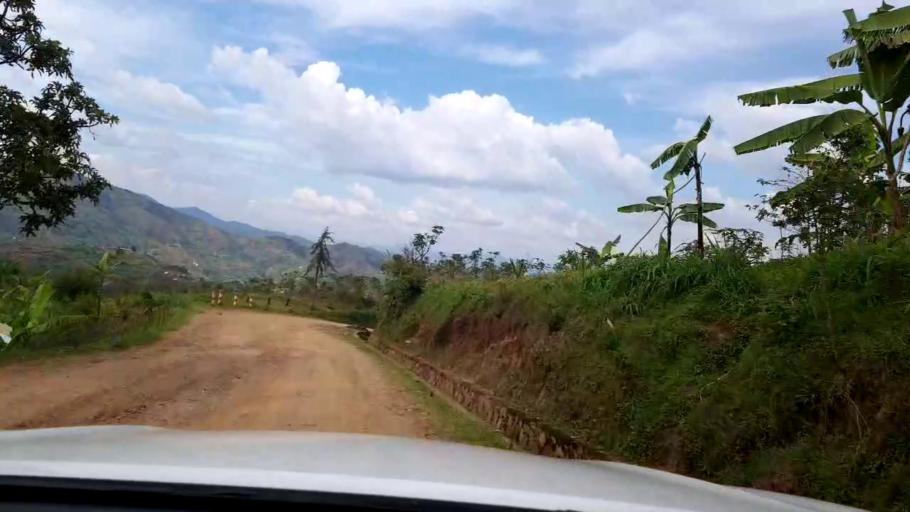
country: RW
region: Southern Province
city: Gitarama
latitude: -1.9827
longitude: 29.7110
